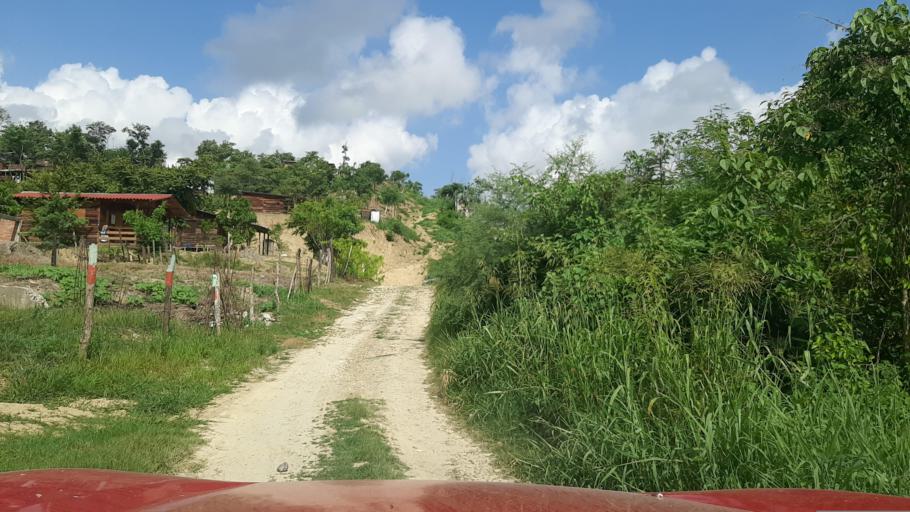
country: MX
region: Veracruz
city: Coatzintla
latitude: 20.5058
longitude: -97.4589
